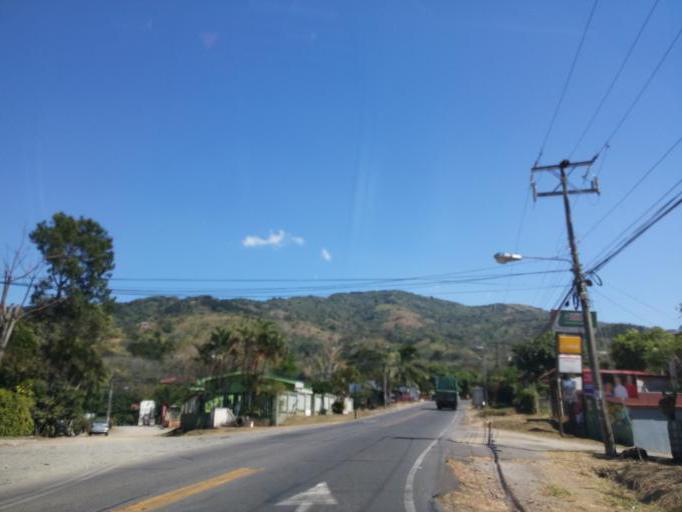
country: CR
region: Heredia
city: Colon
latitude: 9.9105
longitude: -84.2403
